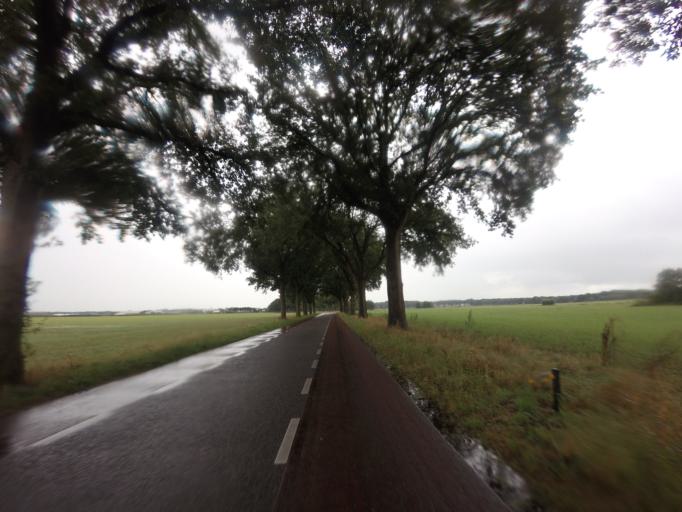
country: NL
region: Drenthe
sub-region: Gemeente Hoogeveen
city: Hoogeveen
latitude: 52.6135
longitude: 6.3968
